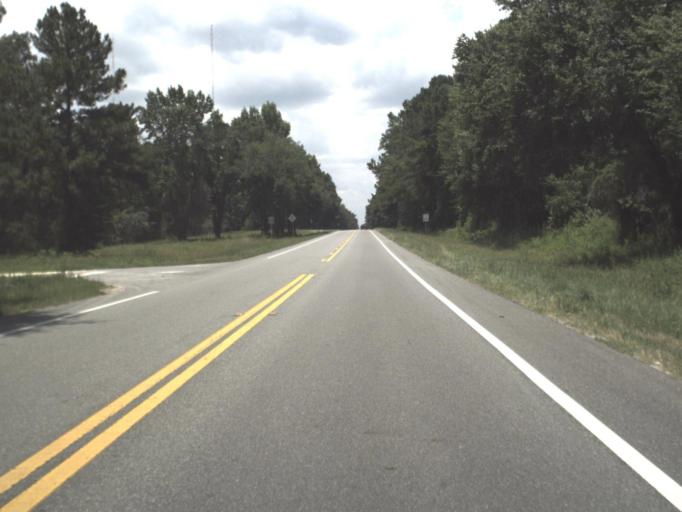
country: US
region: Florida
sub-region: Columbia County
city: Five Points
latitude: 30.2508
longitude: -82.6785
